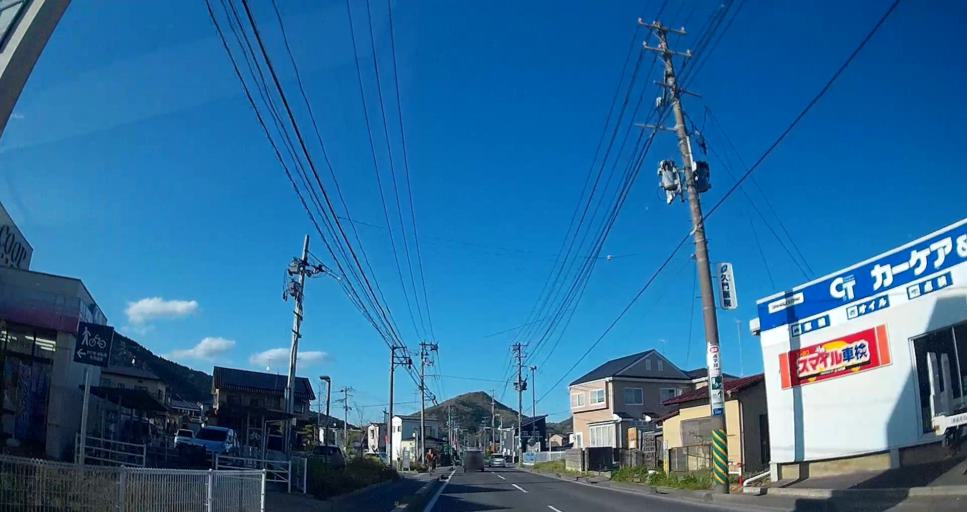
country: JP
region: Miyagi
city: Ishinomaki
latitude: 38.4210
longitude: 141.3676
